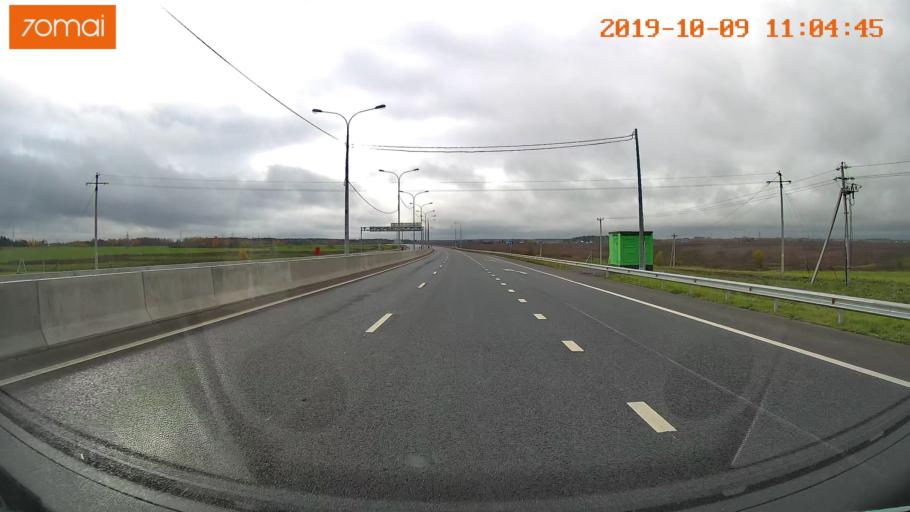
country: RU
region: Vologda
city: Molochnoye
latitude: 59.2087
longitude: 39.7643
